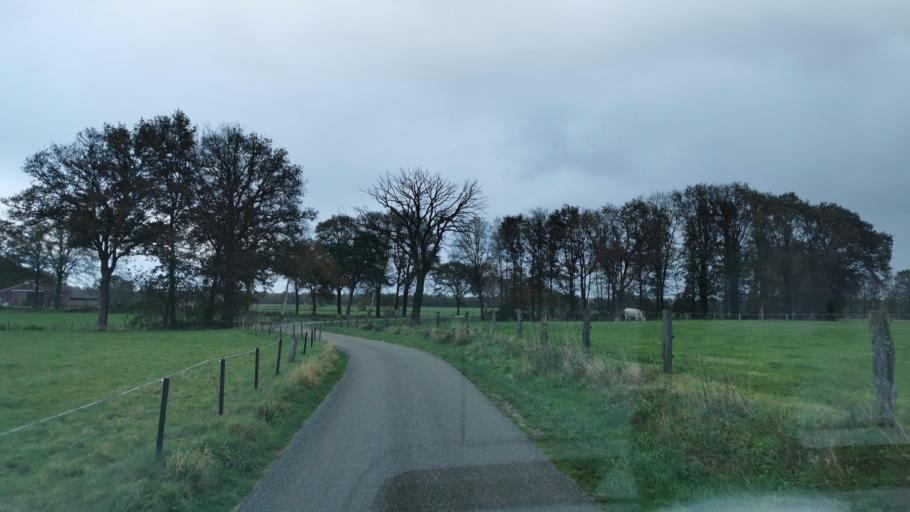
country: NL
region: Overijssel
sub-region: Gemeente Losser
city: Losser
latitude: 52.2510
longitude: 7.0328
